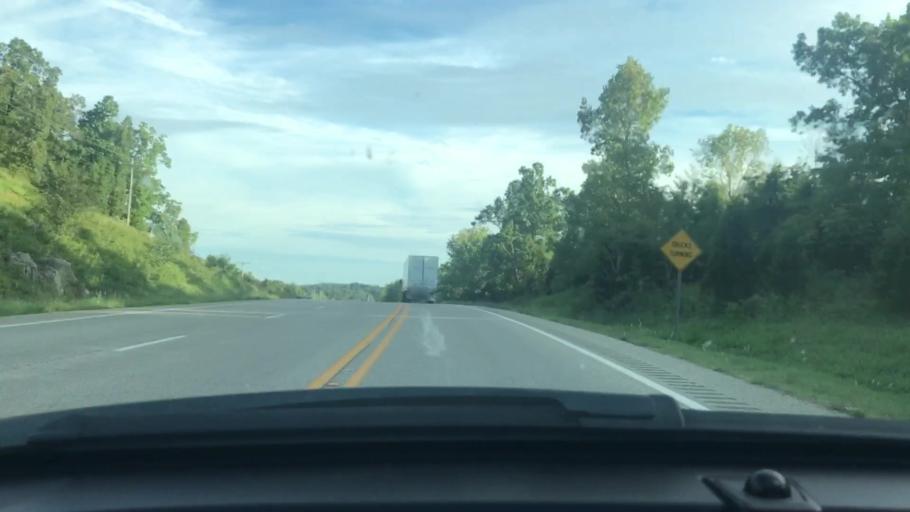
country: US
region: Arkansas
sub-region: Lawrence County
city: Hoxie
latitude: 36.1488
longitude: -91.1602
